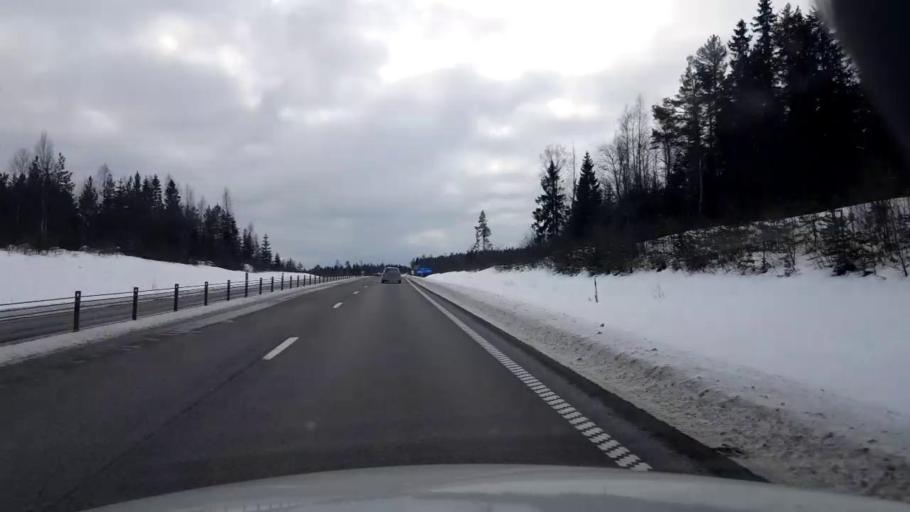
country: SE
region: Vaesternorrland
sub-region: Sundsvalls Kommun
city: Njurundabommen
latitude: 62.1001
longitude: 17.3098
